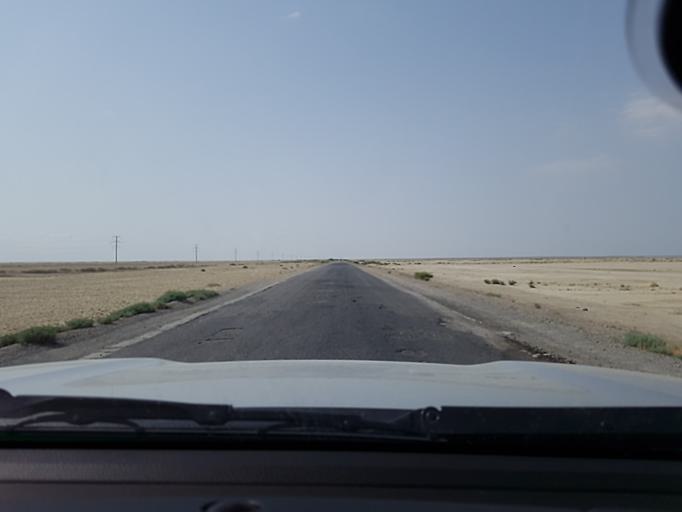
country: TM
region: Balkan
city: Gumdag
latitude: 38.9890
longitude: 54.5869
